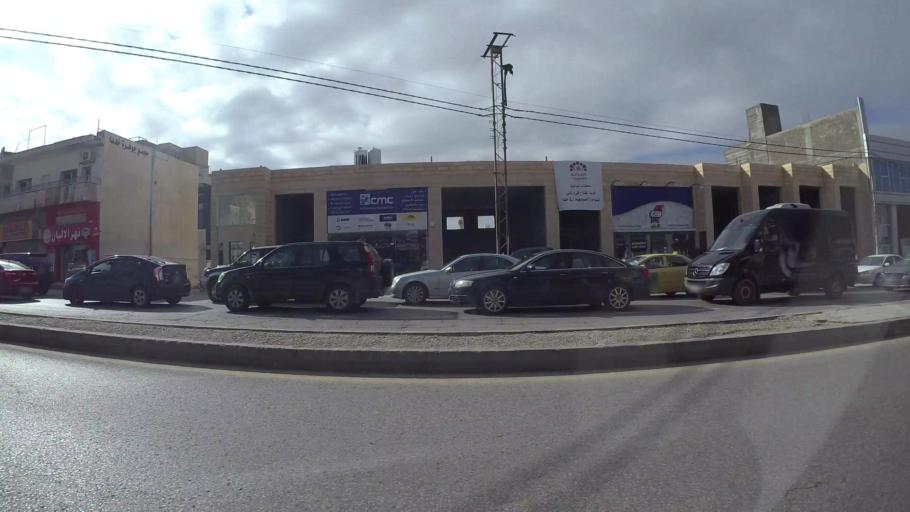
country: JO
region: Amman
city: Al Jubayhah
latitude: 31.9969
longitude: 35.8475
